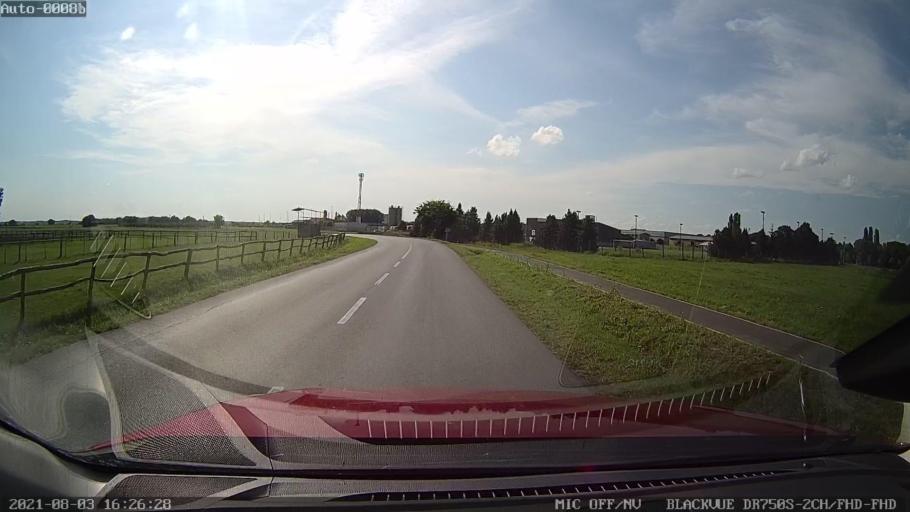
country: HR
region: Osjecko-Baranjska
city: Darda
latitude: 45.6199
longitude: 18.6862
